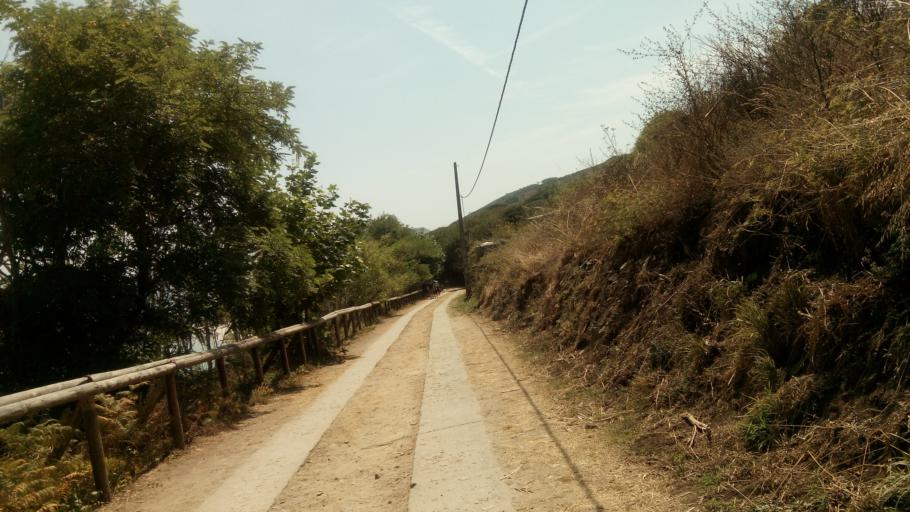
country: ES
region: Galicia
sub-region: Provincia de Pontevedra
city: Sanxenxo
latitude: 42.3756
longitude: -8.9331
